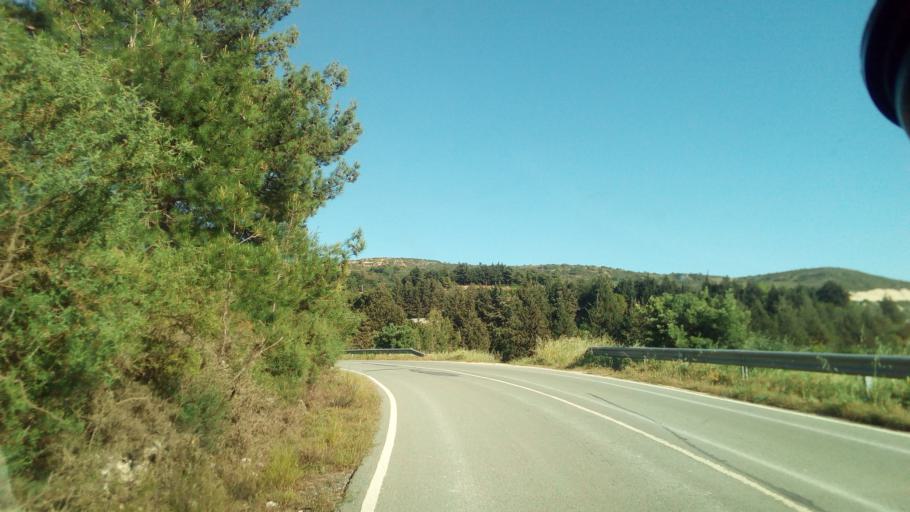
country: CY
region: Limassol
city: Pachna
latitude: 34.8675
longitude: 32.7533
